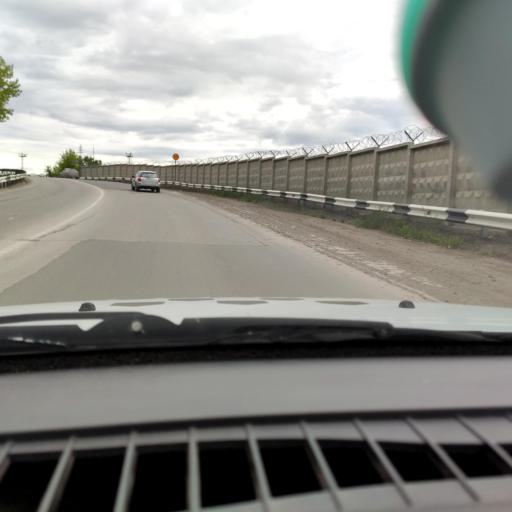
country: RU
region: Perm
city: Chusovoy
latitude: 58.2896
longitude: 57.8135
